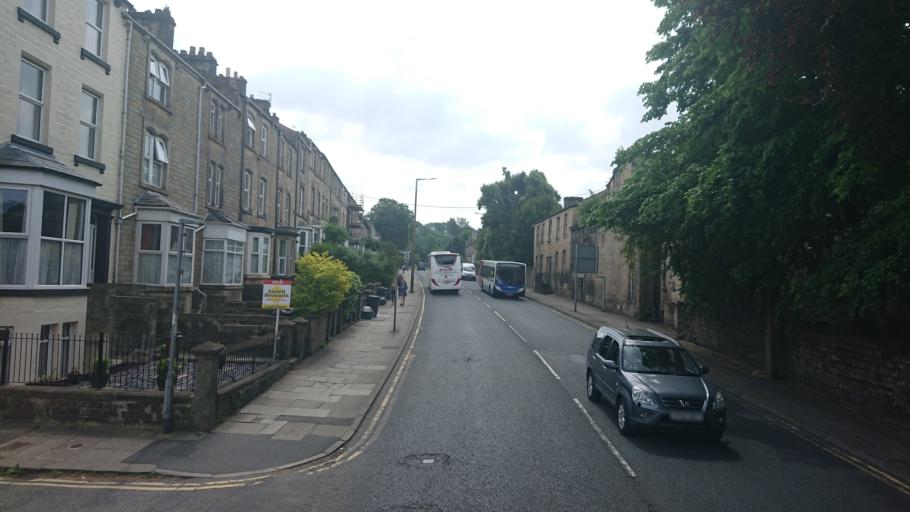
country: GB
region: England
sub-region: Lancashire
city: Lancaster
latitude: 54.0438
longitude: -2.7983
